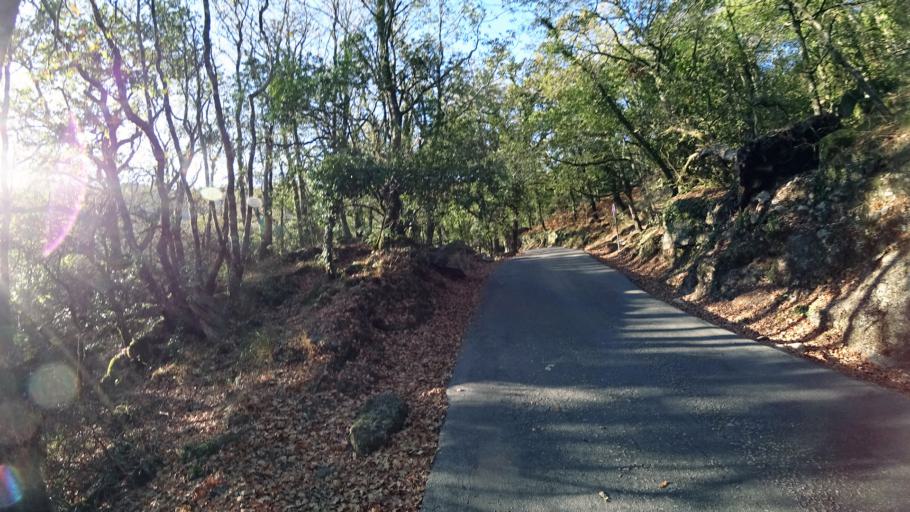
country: ES
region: Galicia
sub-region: Provincia de Ourense
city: Lobios
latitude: 41.8038
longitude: -8.1299
